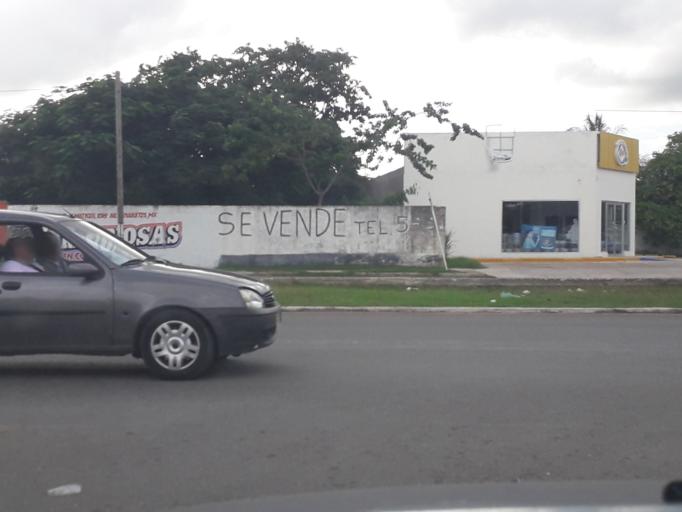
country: MX
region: Yucatan
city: Merida
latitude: 20.9603
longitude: -89.6633
